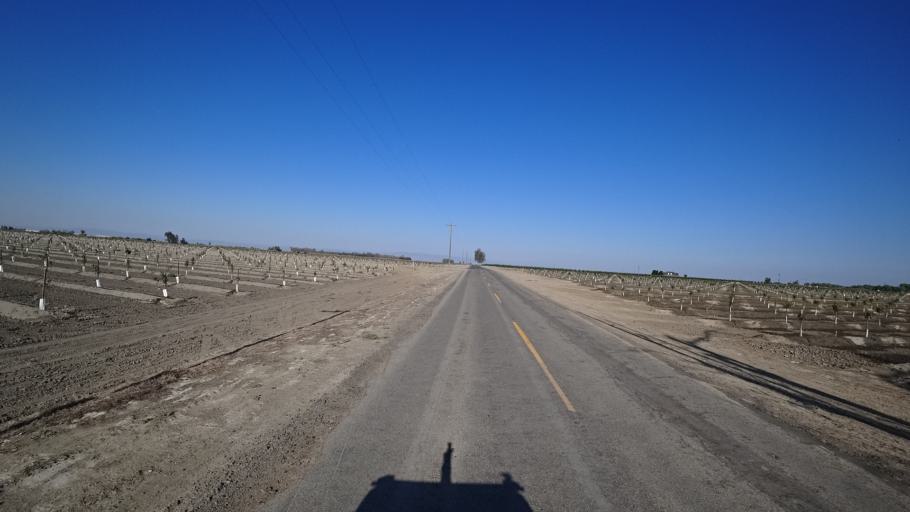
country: US
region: California
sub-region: Fresno County
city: Riverdale
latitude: 36.3802
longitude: -119.9141
